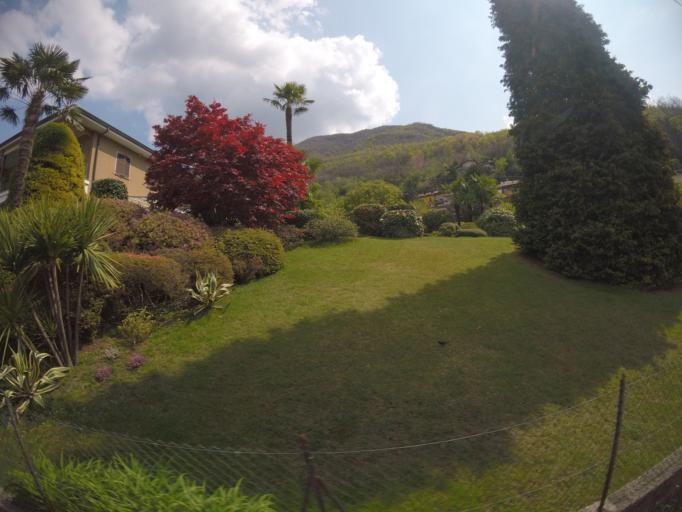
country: IT
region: Piedmont
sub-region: Provincia Verbano-Cusio-Ossola
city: Omegna
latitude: 45.8552
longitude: 8.4073
